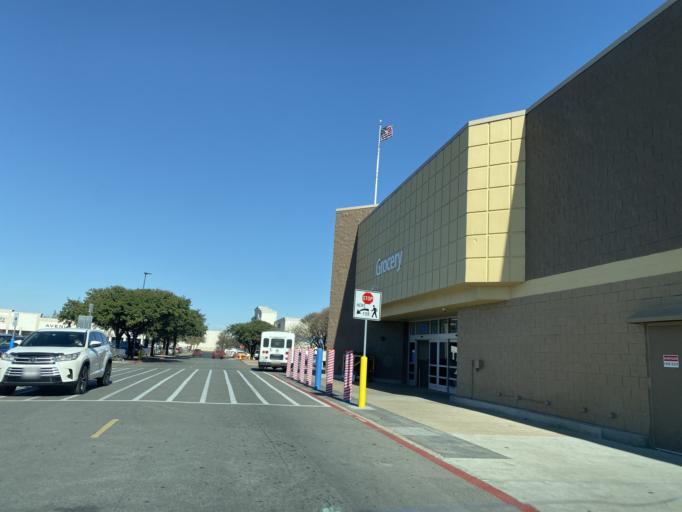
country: US
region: Texas
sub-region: Williamson County
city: Round Rock
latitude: 30.4831
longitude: -97.6705
